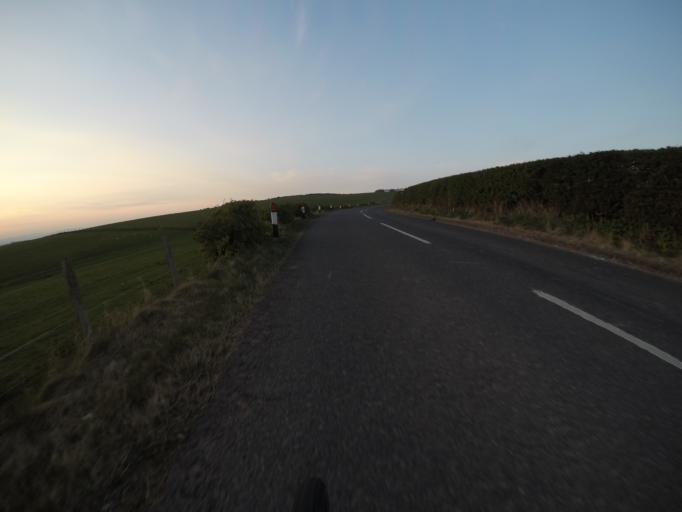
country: GB
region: Scotland
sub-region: South Ayrshire
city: Dundonald
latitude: 55.5558
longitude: -4.6167
